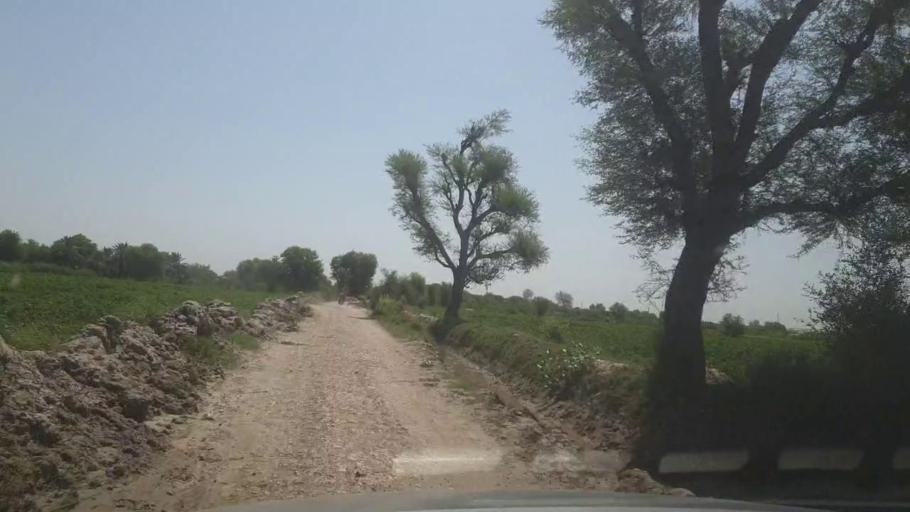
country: PK
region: Sindh
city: Khairpur
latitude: 27.3509
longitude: 69.0595
